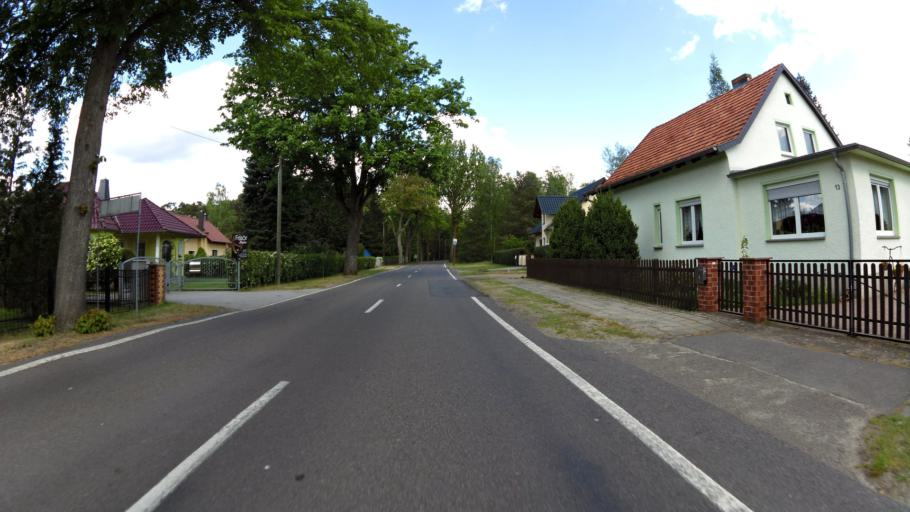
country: DE
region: Brandenburg
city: Wendisch Rietz
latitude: 52.1238
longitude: 13.9503
